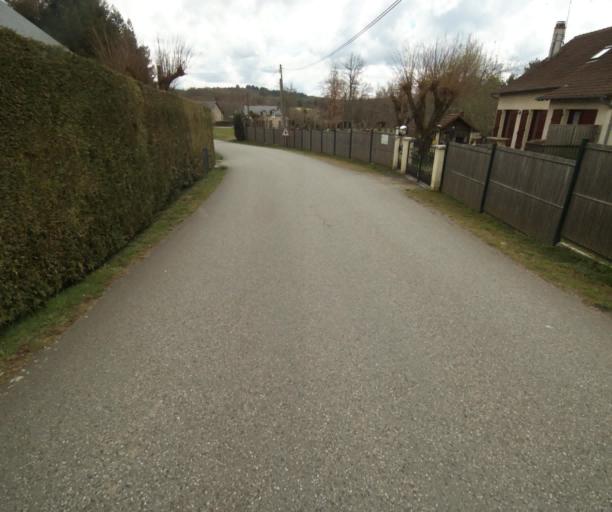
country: FR
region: Limousin
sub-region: Departement de la Correze
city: Correze
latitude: 45.3348
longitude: 1.9201
